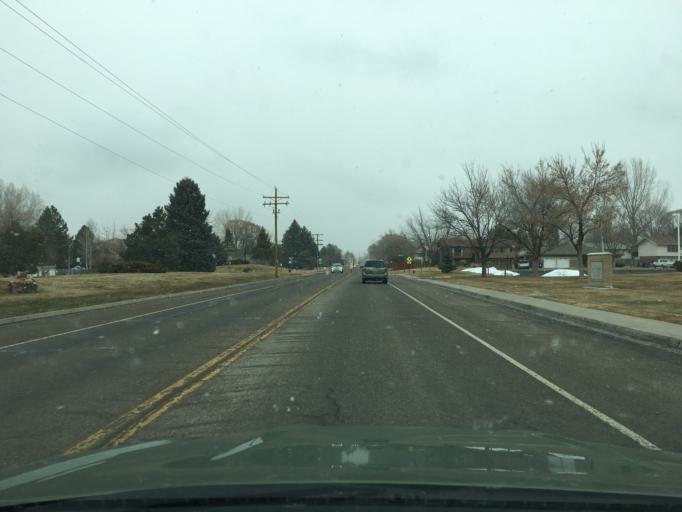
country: US
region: Colorado
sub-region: Montrose County
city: Montrose
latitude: 38.4703
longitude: -107.8566
